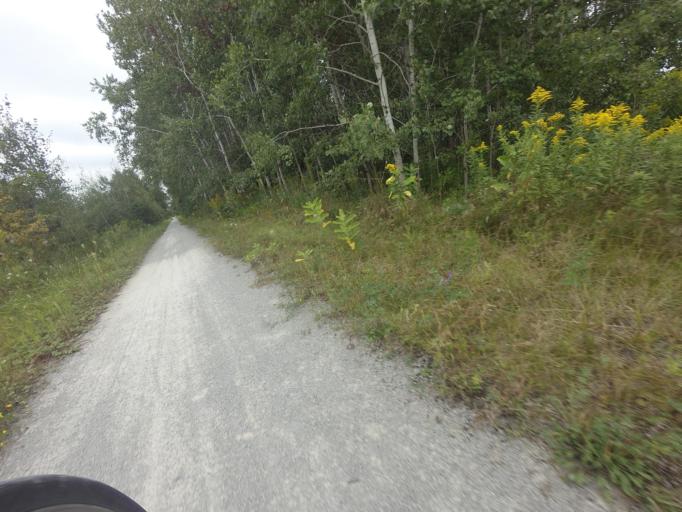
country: CA
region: Ontario
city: Omemee
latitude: 44.3289
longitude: -78.7757
